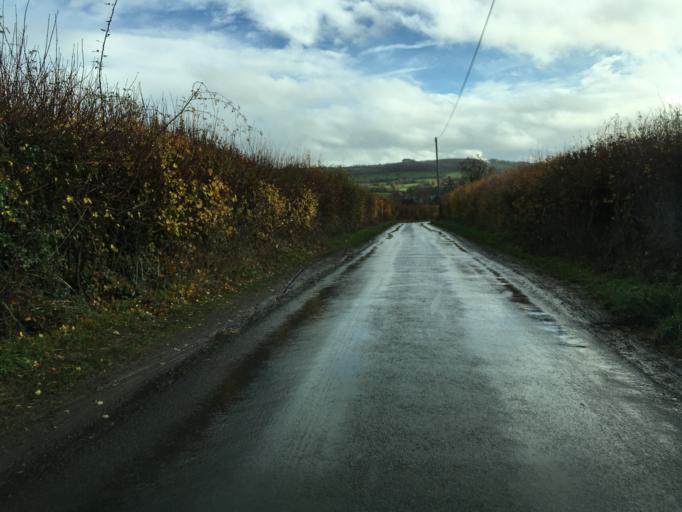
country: GB
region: England
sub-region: South Gloucestershire
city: Pucklechurch
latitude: 51.4722
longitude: -2.4087
